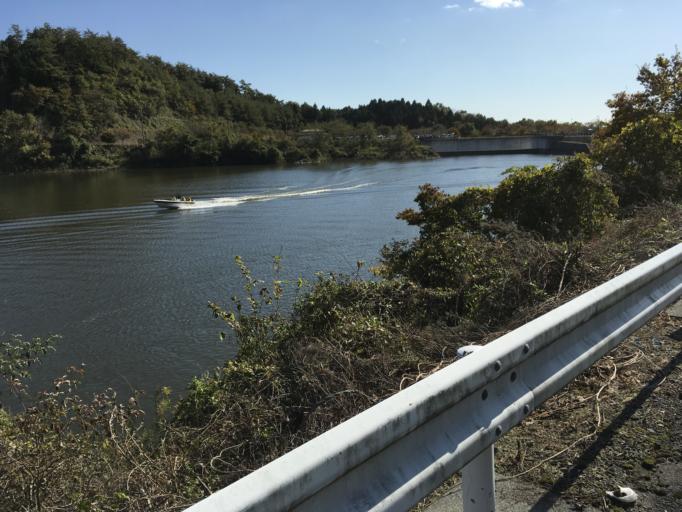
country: JP
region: Iwate
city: Ichinoseki
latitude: 38.7971
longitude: 141.2833
